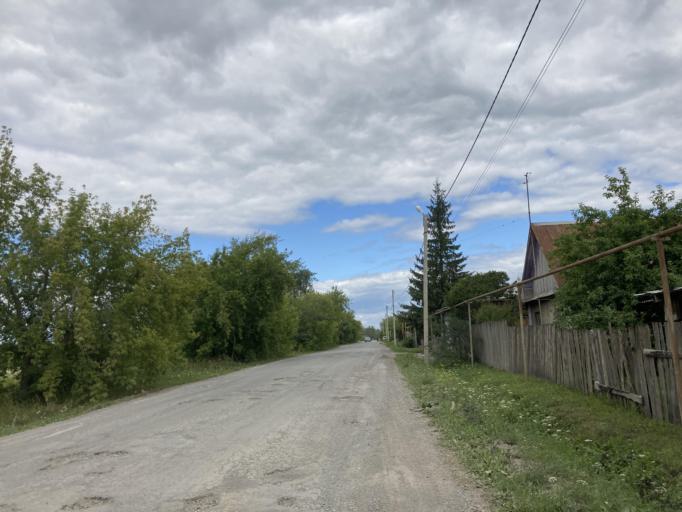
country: RU
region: Sverdlovsk
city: Bogdanovich
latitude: 56.7895
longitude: 62.0670
